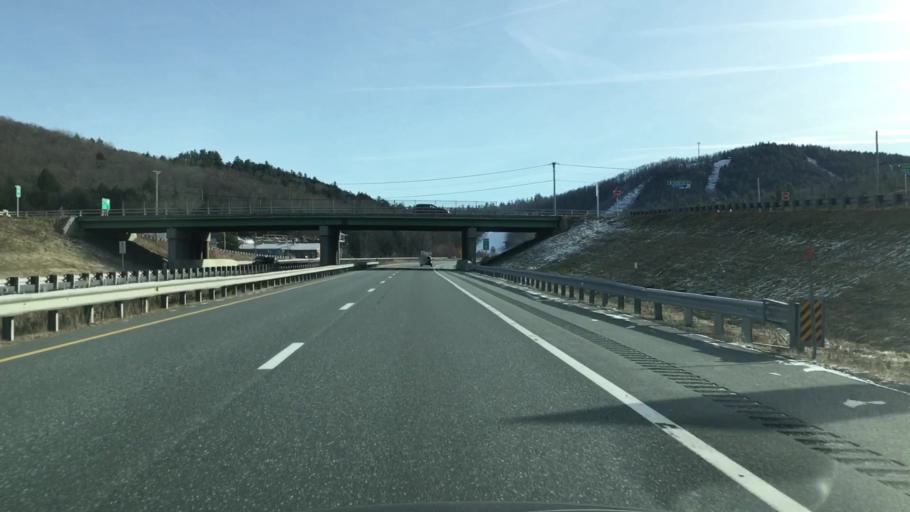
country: US
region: New Hampshire
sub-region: Grafton County
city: Enfield
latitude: 43.6111
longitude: -72.1897
